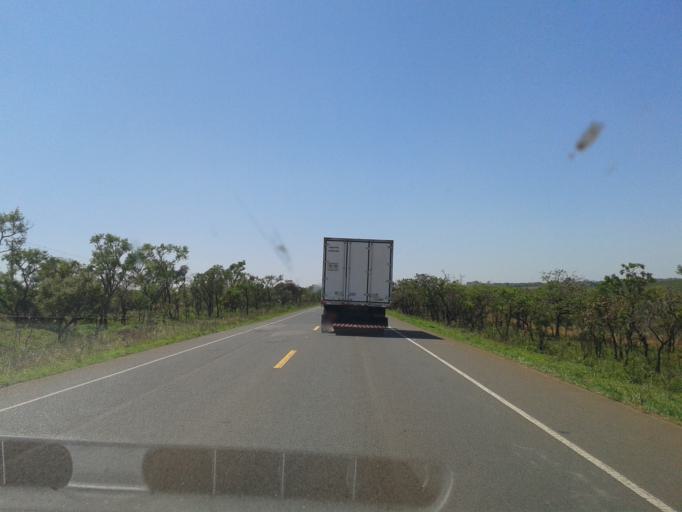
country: BR
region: Minas Gerais
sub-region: Patrocinio
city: Patrocinio
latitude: -19.2831
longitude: -47.4178
